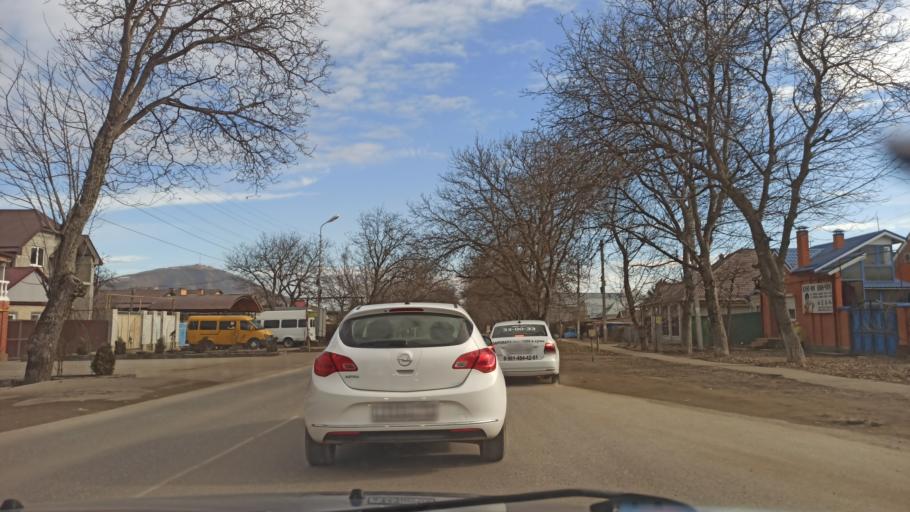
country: RU
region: Stavropol'skiy
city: Svobody
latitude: 44.0328
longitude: 43.0226
